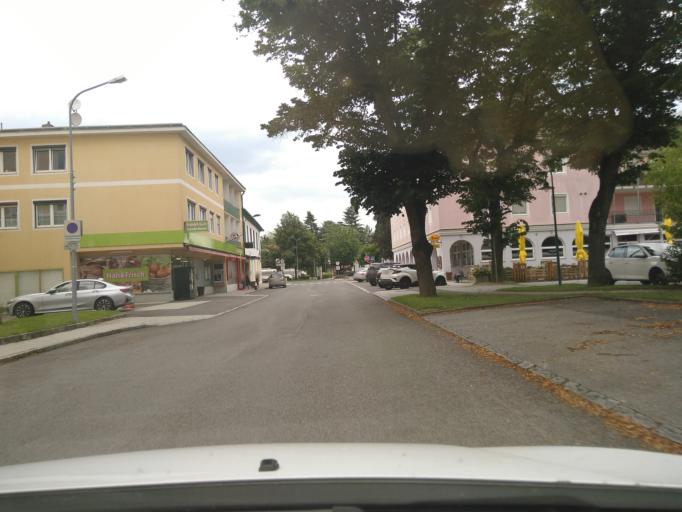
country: AT
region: Burgenland
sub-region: Politischer Bezirk Oberwart
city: Oberschutzen
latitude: 47.3500
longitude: 16.2075
